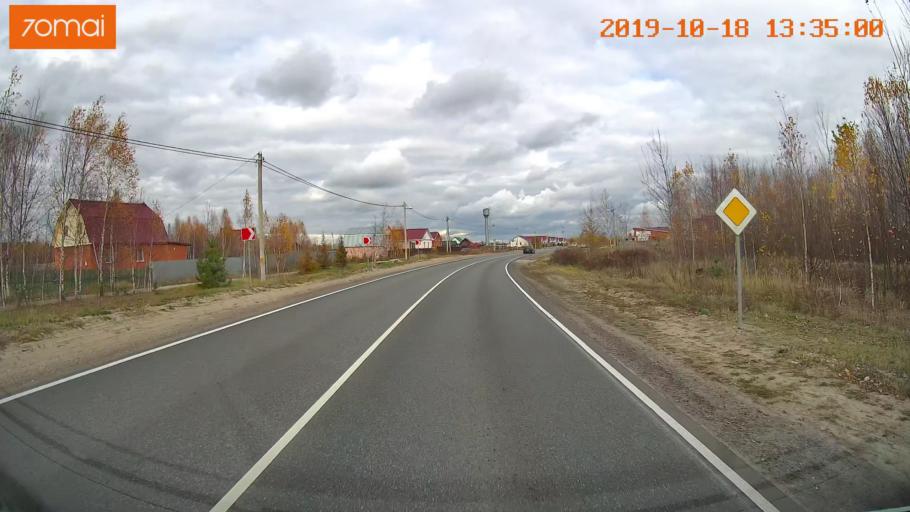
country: RU
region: Rjazan
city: Solotcha
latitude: 54.8579
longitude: 39.9616
